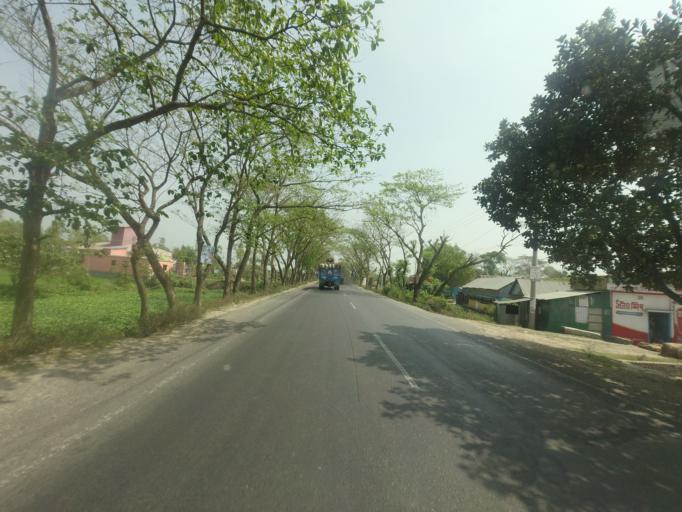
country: BD
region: Dhaka
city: Bhairab Bazar
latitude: 24.0478
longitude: 91.0925
